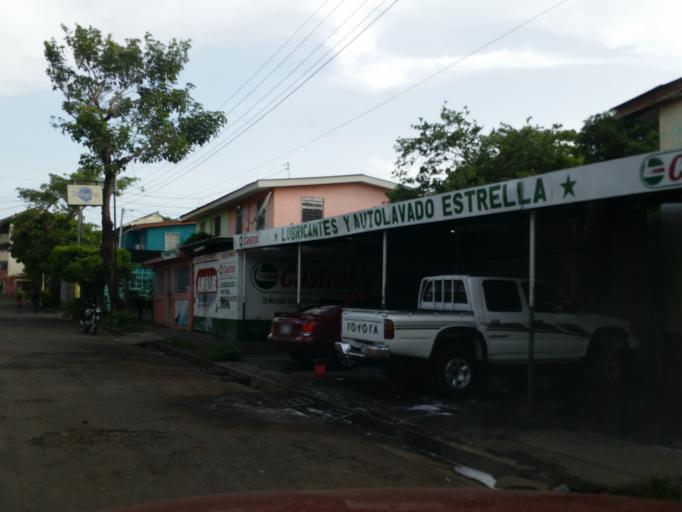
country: NI
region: Managua
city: Managua
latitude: 12.1544
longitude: -86.2777
